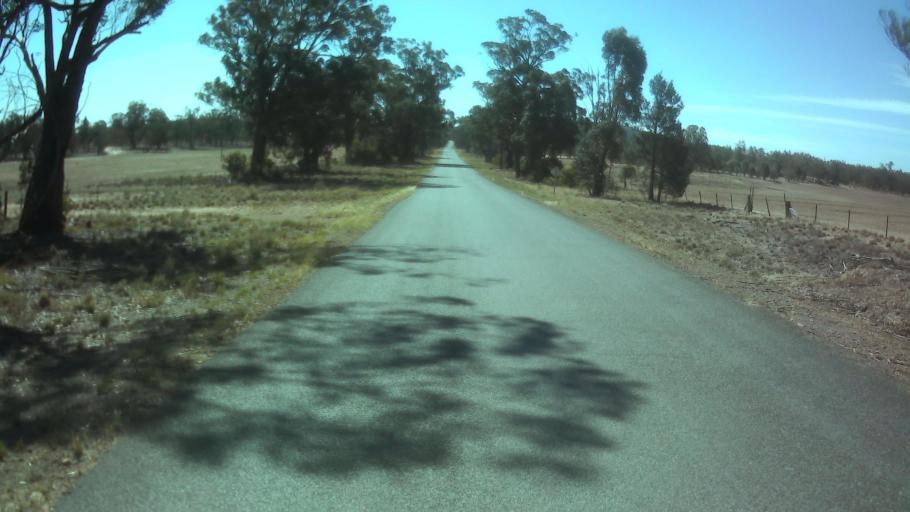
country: AU
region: New South Wales
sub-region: Weddin
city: Grenfell
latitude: -33.8042
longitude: 147.8961
